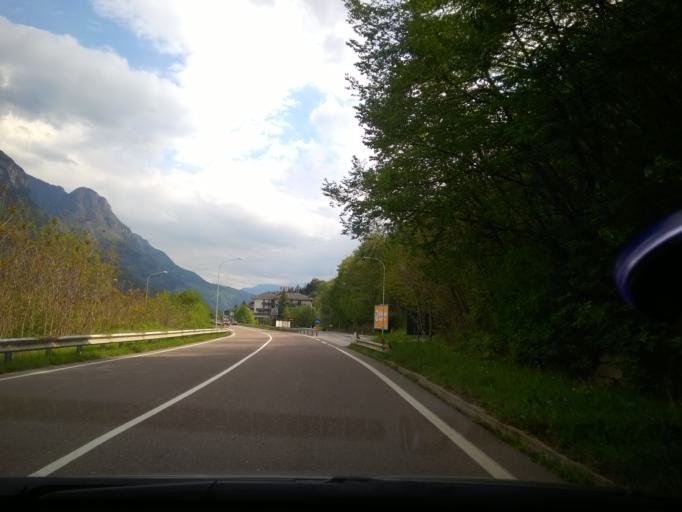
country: IT
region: Veneto
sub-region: Provincia di Belluno
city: Longarone
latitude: 46.2506
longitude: 12.2982
